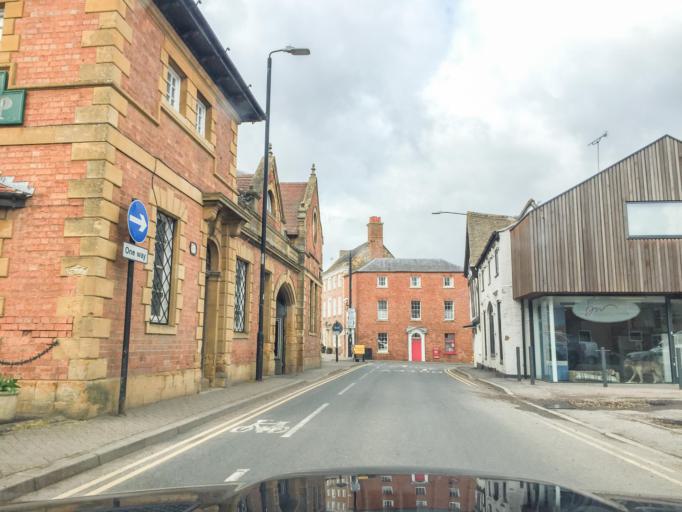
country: GB
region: England
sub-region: Warwickshire
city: Shipston on Stour
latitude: 52.0621
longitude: -1.6243
